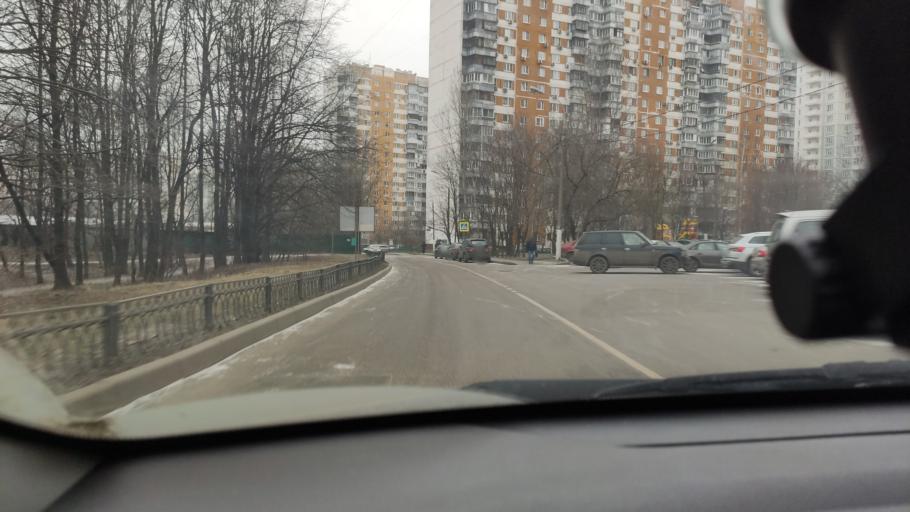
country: RU
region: Moscow
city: Chertanovo Yuzhnoye
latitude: 55.5932
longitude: 37.5934
